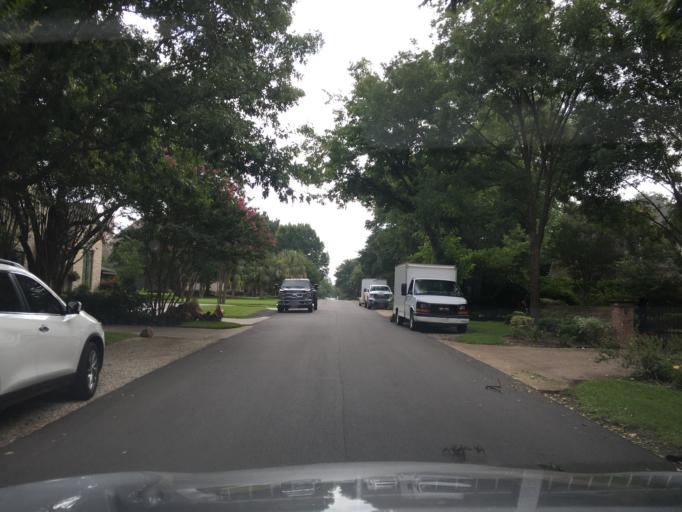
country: US
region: Texas
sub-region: Dallas County
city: University Park
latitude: 32.8833
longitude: -96.7948
